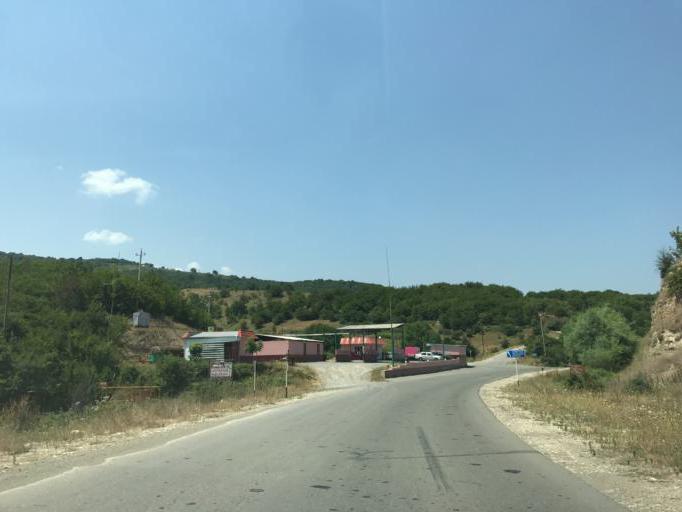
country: AZ
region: Tartar Rayon
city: Martakert
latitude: 40.1399
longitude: 46.5869
